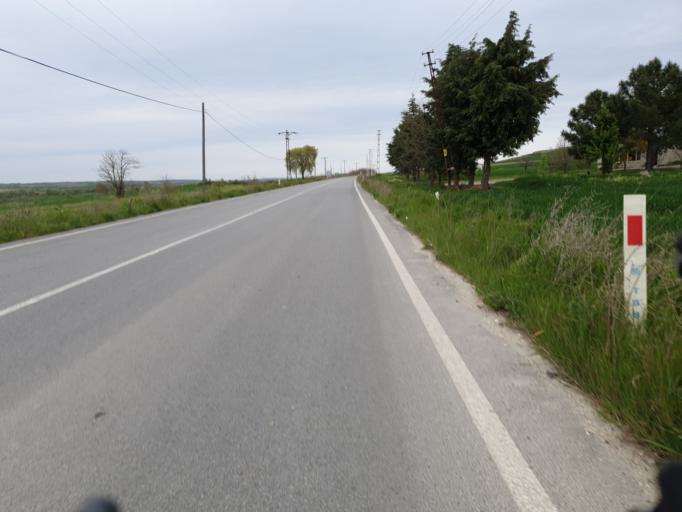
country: TR
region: Tekirdag
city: Velimese
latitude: 41.3479
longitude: 27.8371
